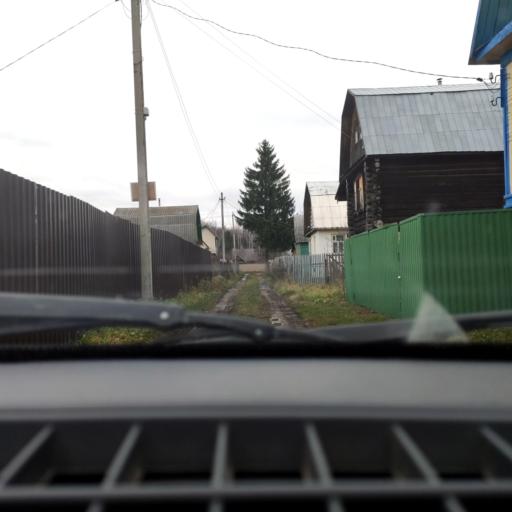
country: RU
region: Bashkortostan
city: Avdon
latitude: 54.6245
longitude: 55.7186
